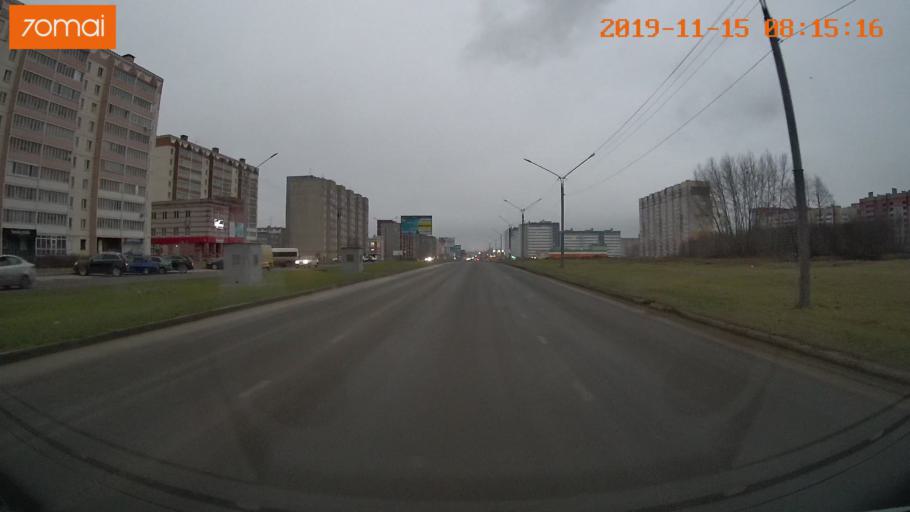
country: RU
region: Vologda
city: Cherepovets
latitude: 59.0809
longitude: 37.9233
